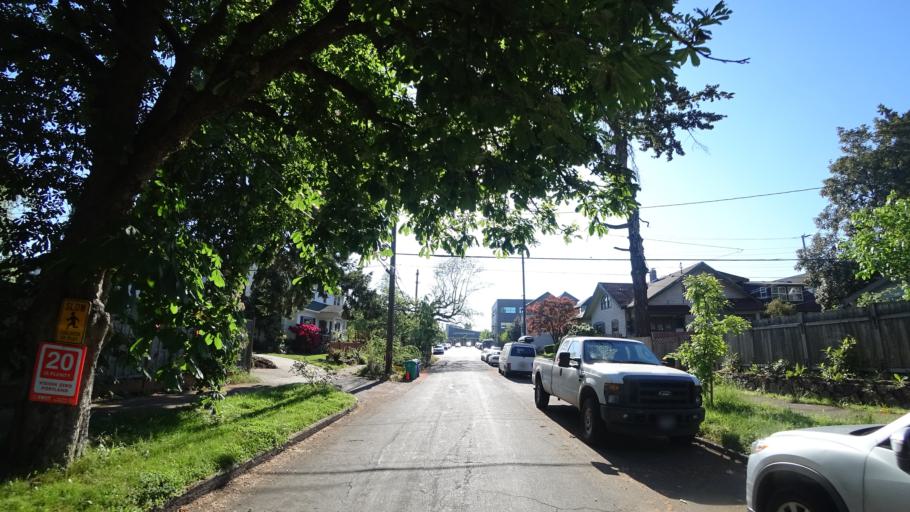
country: US
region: Oregon
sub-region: Multnomah County
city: Portland
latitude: 45.5616
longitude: -122.6634
